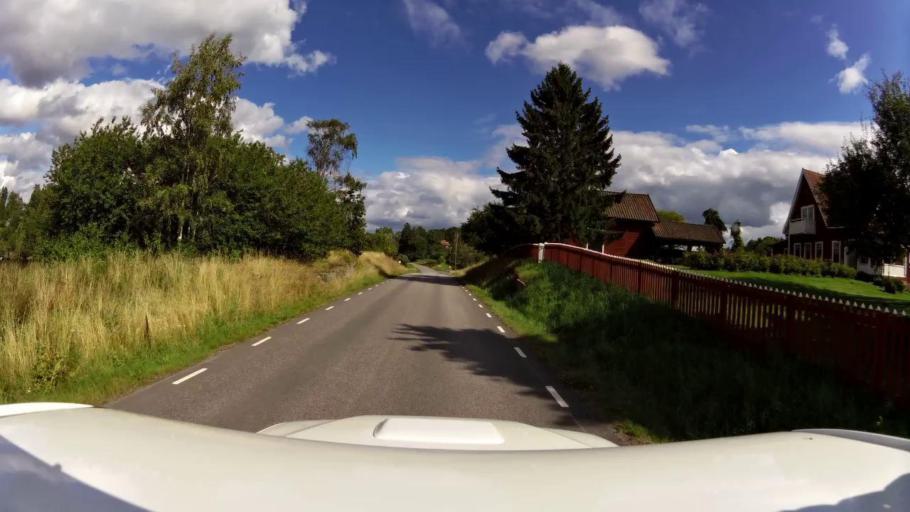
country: SE
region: OEstergoetland
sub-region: Kinda Kommun
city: Rimforsa
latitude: 58.2280
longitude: 15.7237
